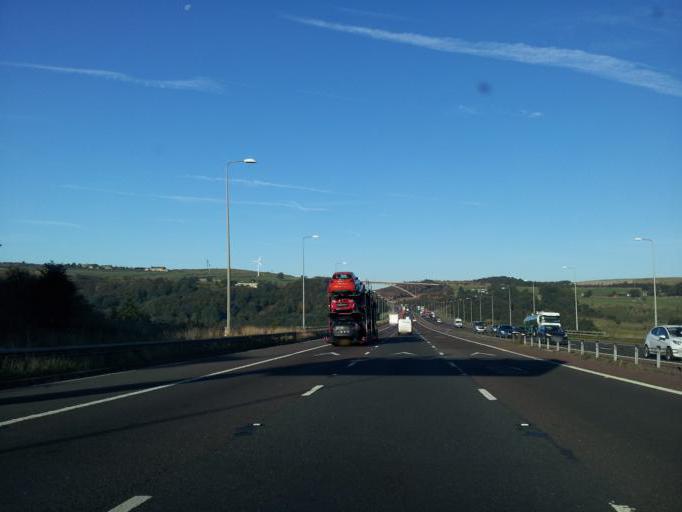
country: GB
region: England
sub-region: Calderdale
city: Ripponden
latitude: 53.6461
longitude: -1.9166
